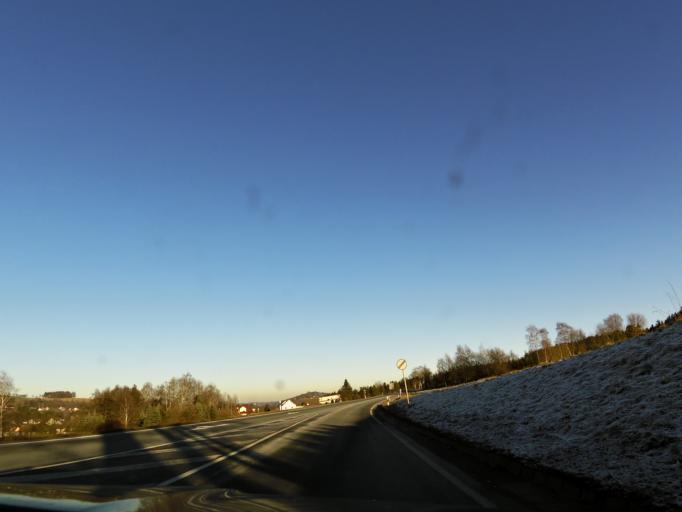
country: DE
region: Bavaria
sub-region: Upper Franconia
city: Trostau
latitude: 50.0171
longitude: 11.9628
